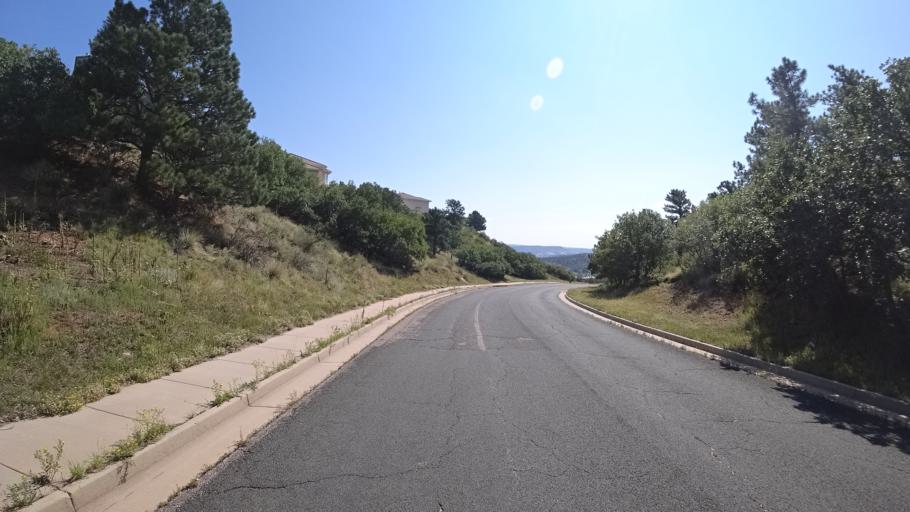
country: US
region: Colorado
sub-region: El Paso County
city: Manitou Springs
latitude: 38.9165
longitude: -104.8719
